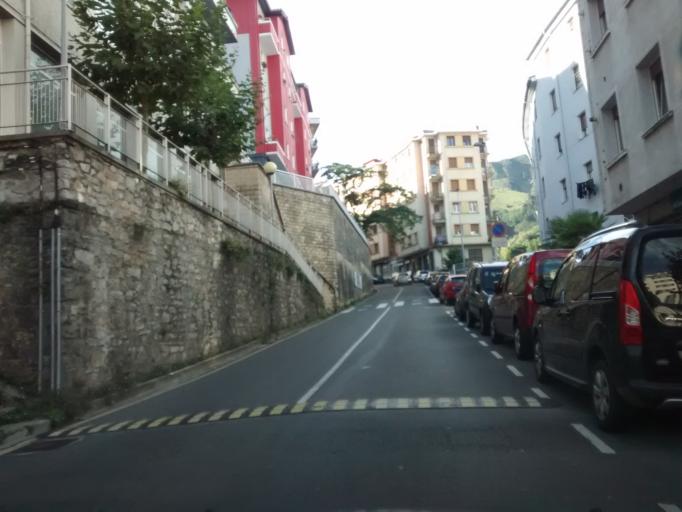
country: ES
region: Basque Country
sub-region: Provincia de Guipuzcoa
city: Eibar
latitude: 43.1816
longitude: -2.4722
